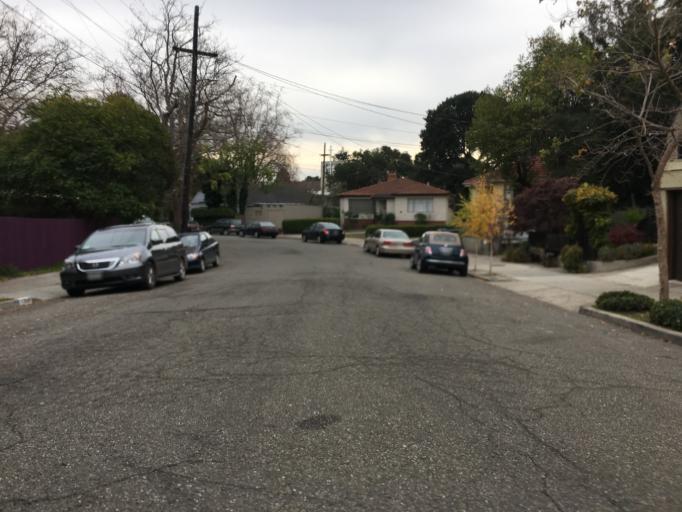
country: US
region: California
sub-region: Alameda County
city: Berkeley
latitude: 37.8837
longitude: -122.2795
